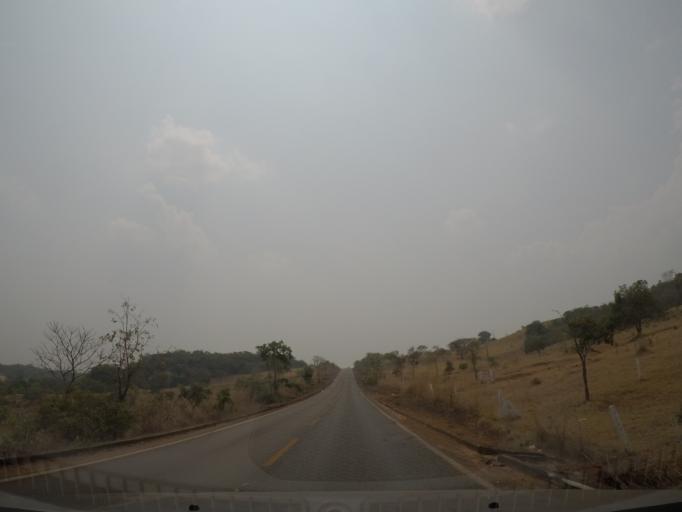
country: BR
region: Goias
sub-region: Pirenopolis
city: Pirenopolis
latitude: -15.9209
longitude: -48.8549
